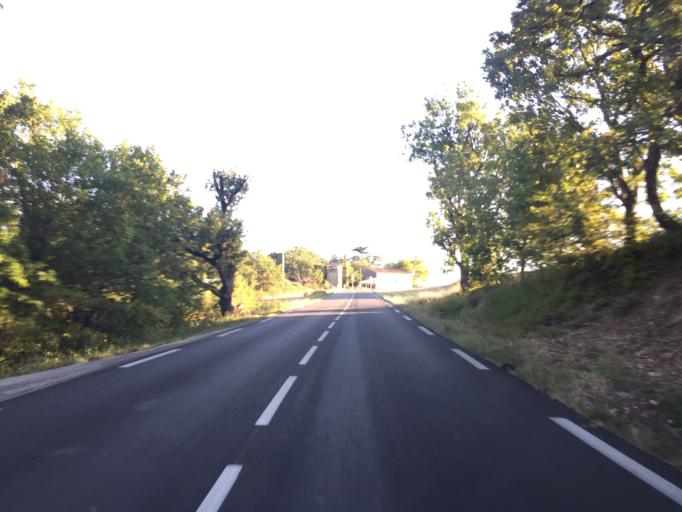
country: FR
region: Provence-Alpes-Cote d'Azur
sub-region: Departement des Alpes-de-Haute-Provence
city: Reillanne
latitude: 43.8882
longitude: 5.7205
